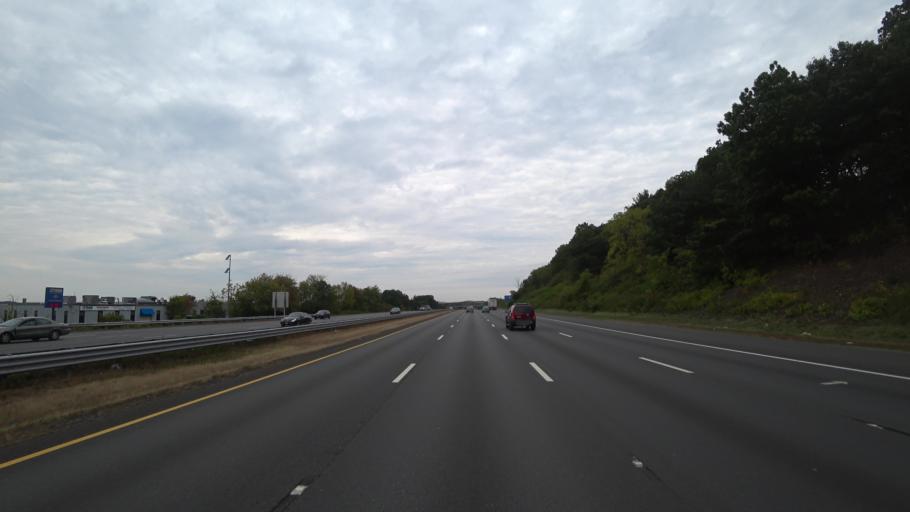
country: US
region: Massachusetts
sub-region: Middlesex County
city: Reading
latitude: 42.5129
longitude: -71.1269
